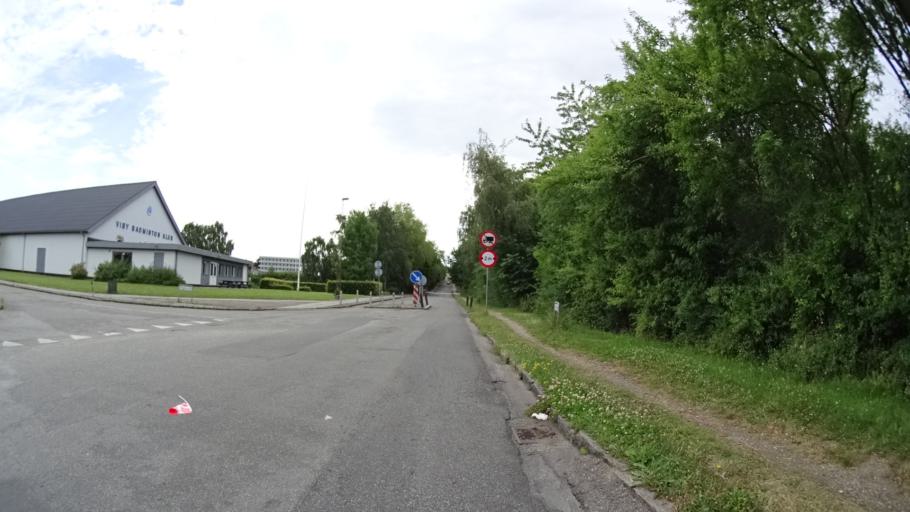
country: DK
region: Central Jutland
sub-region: Arhus Kommune
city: Stavtrup
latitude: 56.1268
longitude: 10.1486
